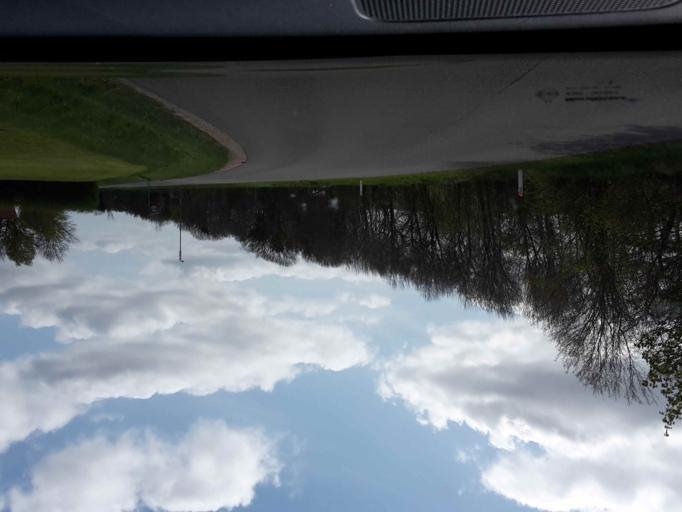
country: DK
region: South Denmark
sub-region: Varde Kommune
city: Olgod
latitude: 55.8051
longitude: 8.6207
